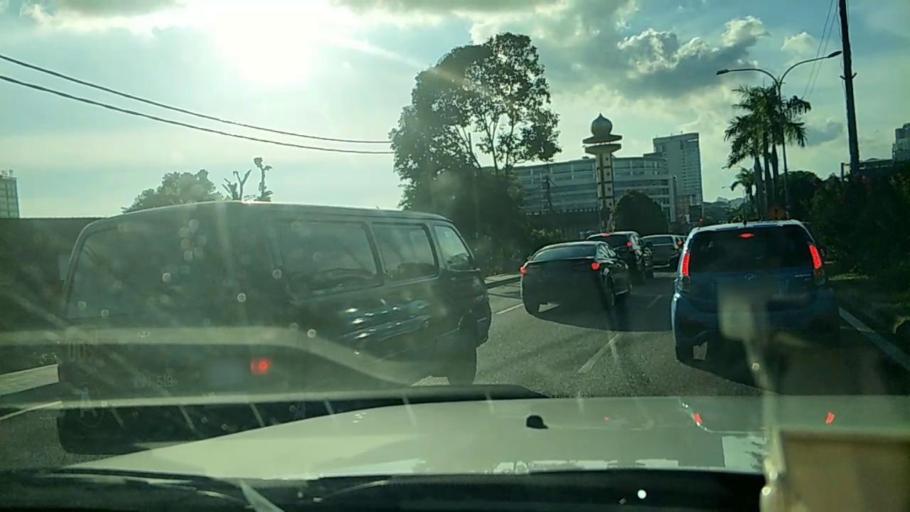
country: MY
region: Selangor
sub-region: Petaling
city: Petaling Jaya
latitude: 3.1118
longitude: 101.6352
